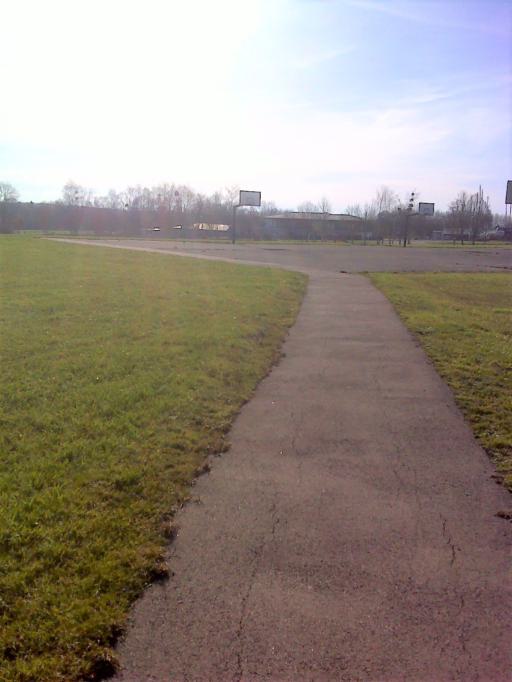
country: FR
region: Champagne-Ardenne
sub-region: Departement de l'Aube
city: Lusigny-sur-Barse
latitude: 48.2574
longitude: 4.3407
